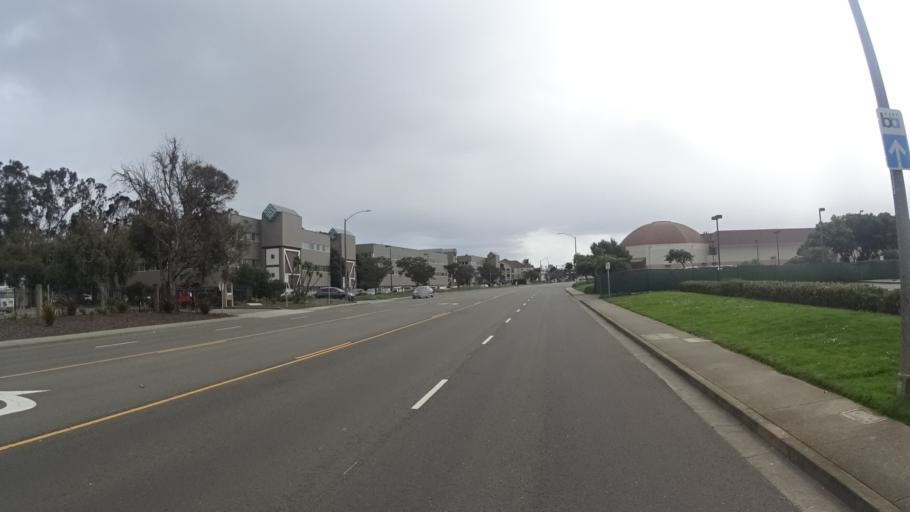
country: US
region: California
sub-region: San Mateo County
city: San Bruno
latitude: 37.6436
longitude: -122.4213
